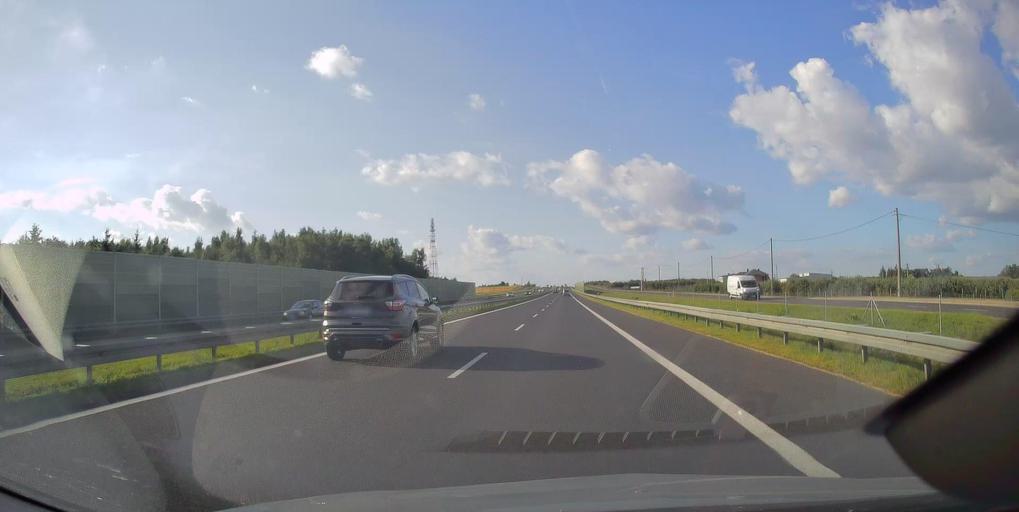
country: PL
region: Masovian Voivodeship
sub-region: Powiat bialobrzeski
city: Promna
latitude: 51.7095
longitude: 20.9260
